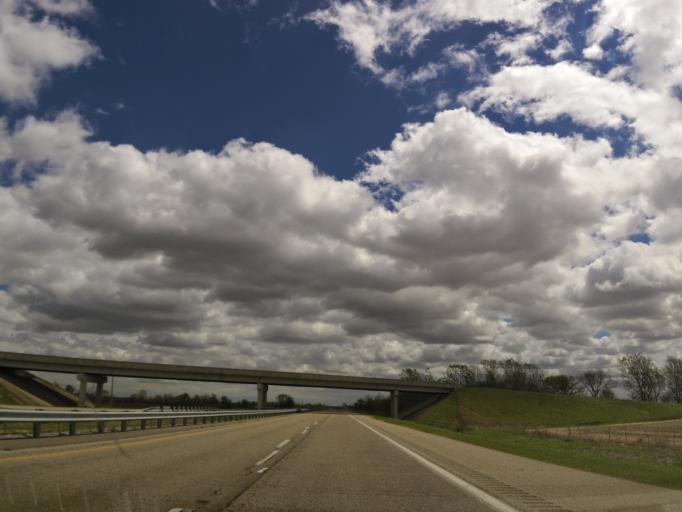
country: US
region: Arkansas
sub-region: Poinsett County
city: Trumann
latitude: 35.6550
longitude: -90.5372
